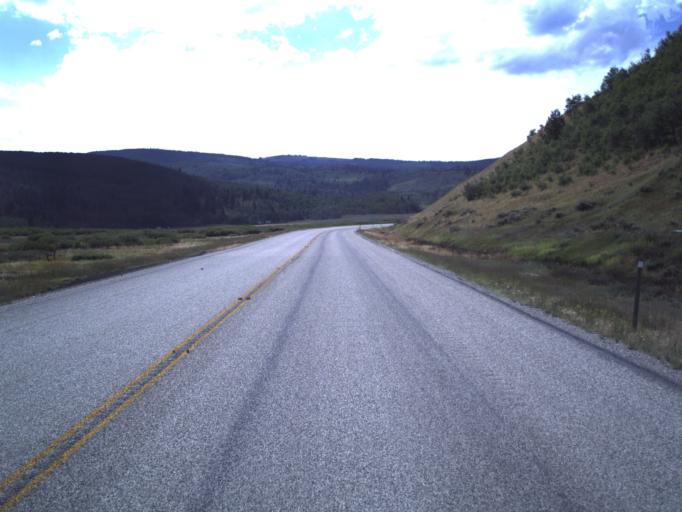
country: US
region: Utah
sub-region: Wasatch County
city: Heber
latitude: 40.2824
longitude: -111.2328
